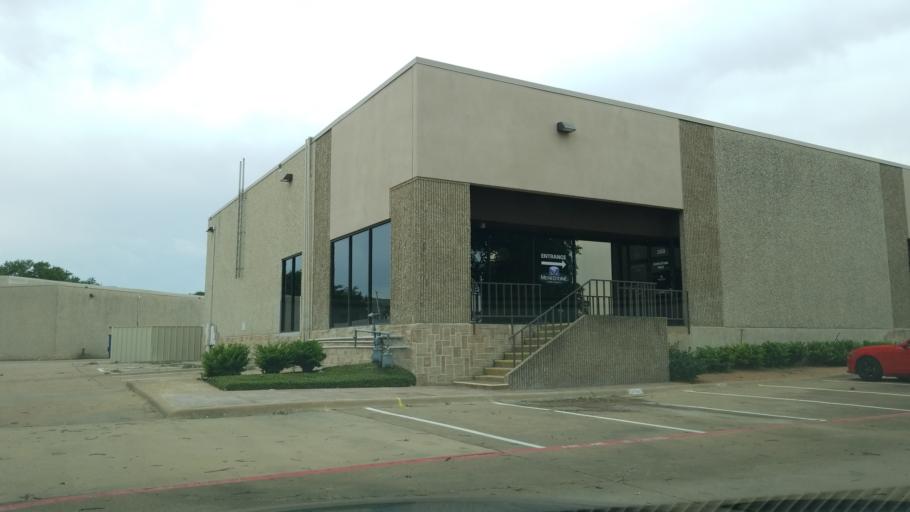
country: US
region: Texas
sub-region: Dallas County
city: Coppell
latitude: 32.8915
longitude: -96.9868
